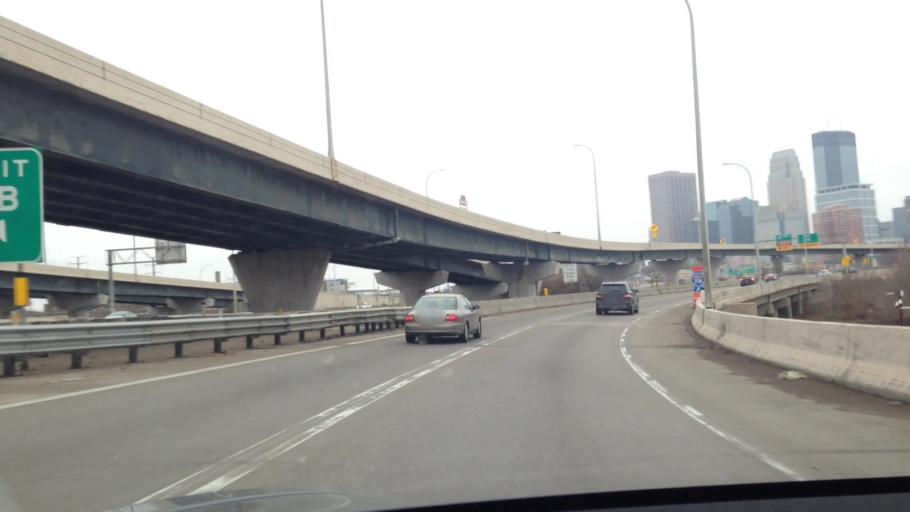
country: US
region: Minnesota
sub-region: Hennepin County
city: Minneapolis
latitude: 44.9739
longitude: -93.2923
